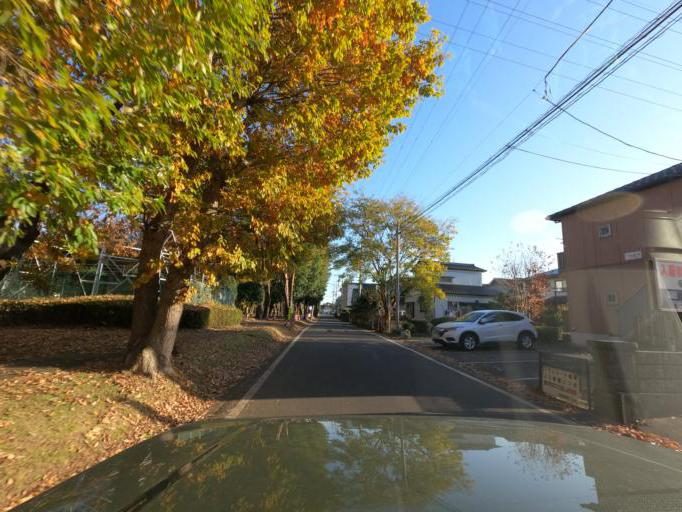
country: JP
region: Ibaraki
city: Naka
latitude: 36.0507
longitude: 140.1299
